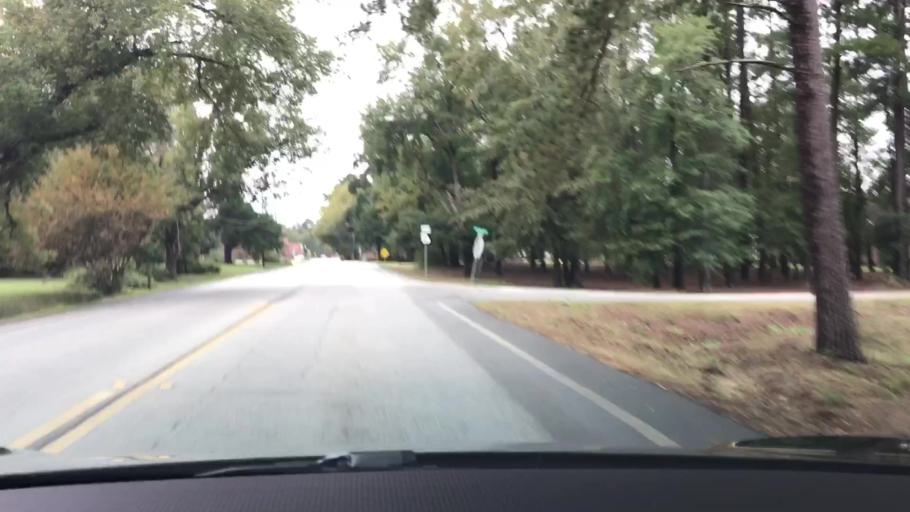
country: US
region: Georgia
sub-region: Jefferson County
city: Wrens
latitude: 33.2182
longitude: -82.4665
